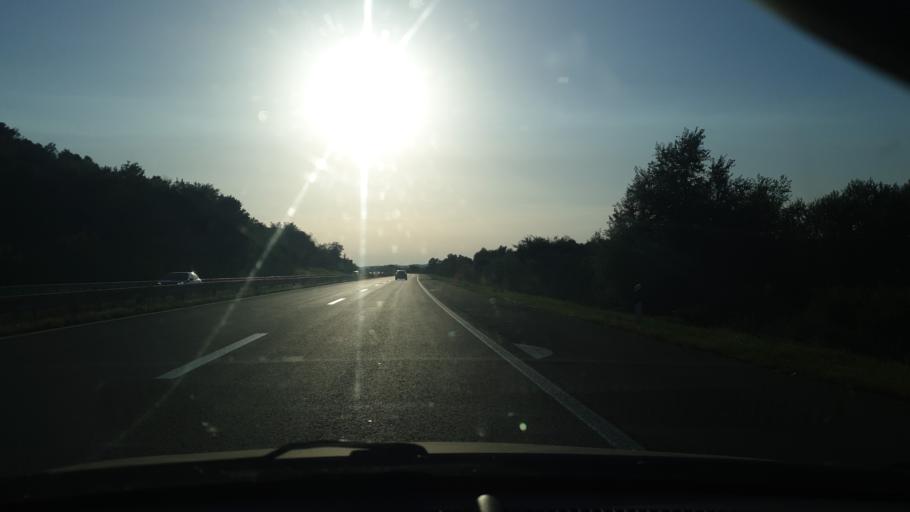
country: RS
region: Central Serbia
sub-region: Belgrade
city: Grocka
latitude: 44.5802
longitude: 20.7868
